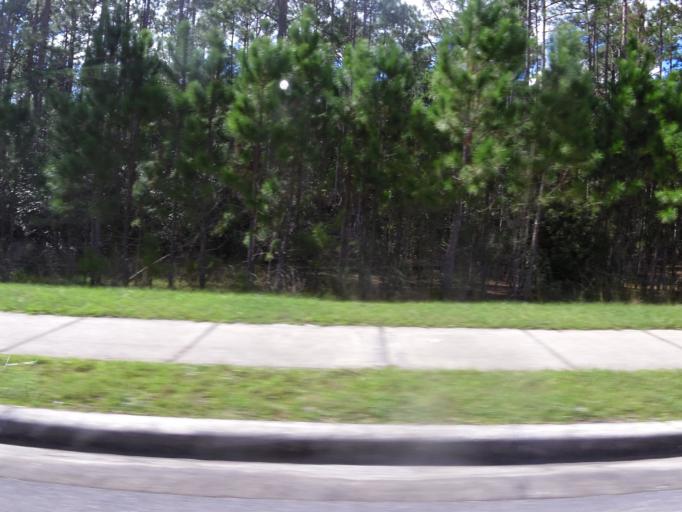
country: US
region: Florida
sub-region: Saint Johns County
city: Fruit Cove
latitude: 30.0648
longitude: -81.5317
